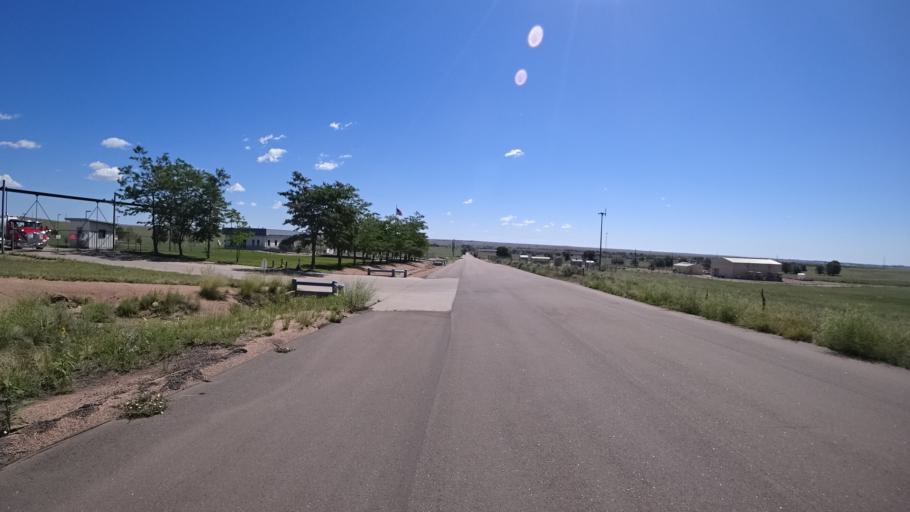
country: US
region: Colorado
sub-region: El Paso County
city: Security-Widefield
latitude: 38.7810
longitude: -104.6761
